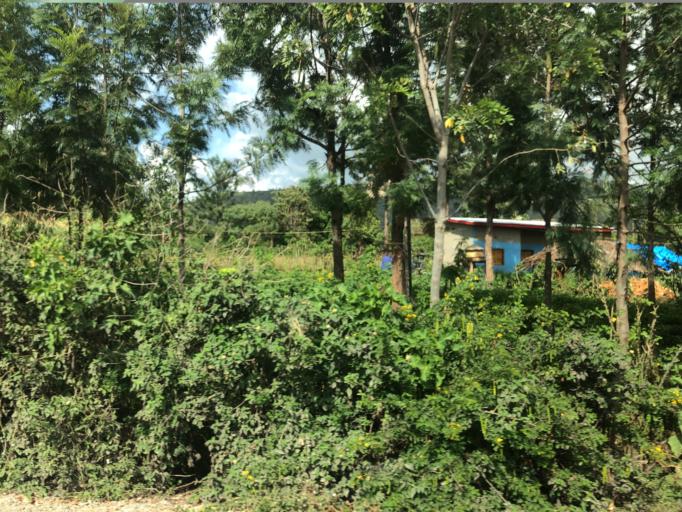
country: ET
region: Southern Nations, Nationalities, and People's Region
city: Bako
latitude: 5.7431
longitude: 36.6002
